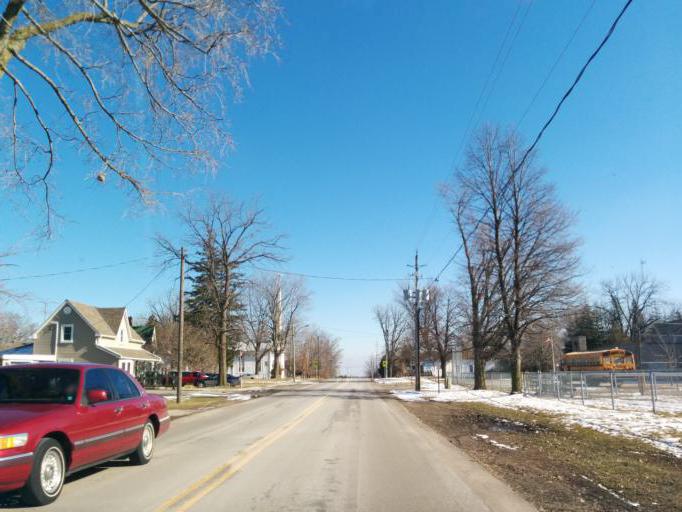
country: CA
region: Ontario
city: Brant
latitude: 43.0226
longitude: -80.3783
